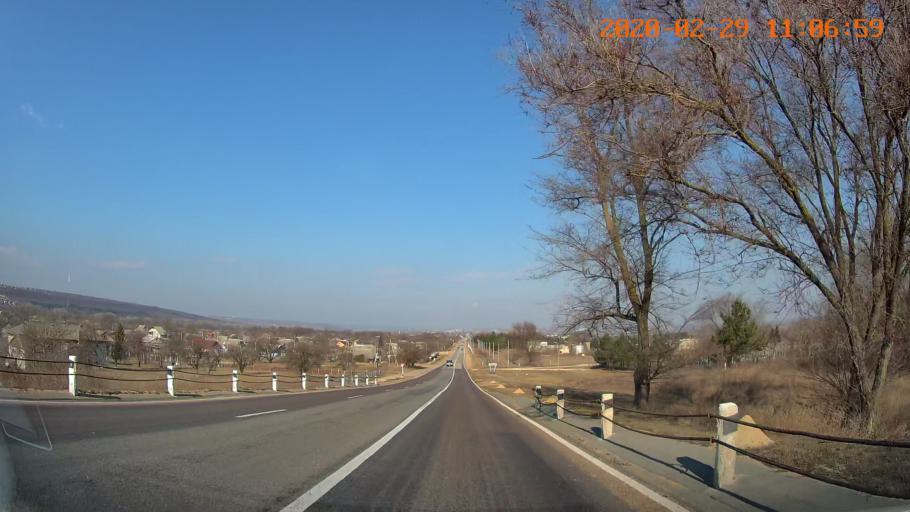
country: MD
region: Criuleni
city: Criuleni
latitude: 47.2207
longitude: 29.1854
